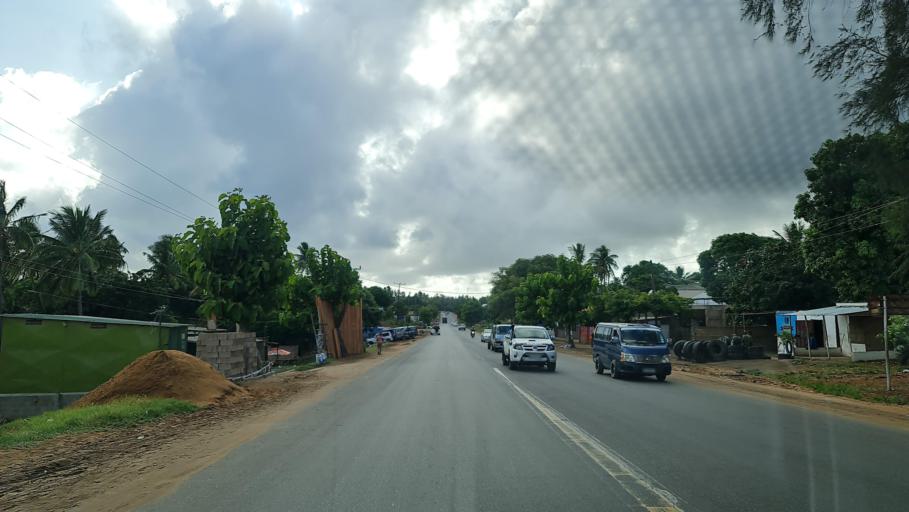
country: MZ
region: Gaza
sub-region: Xai-Xai District
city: Xai-Xai
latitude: -25.0563
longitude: 33.6729
